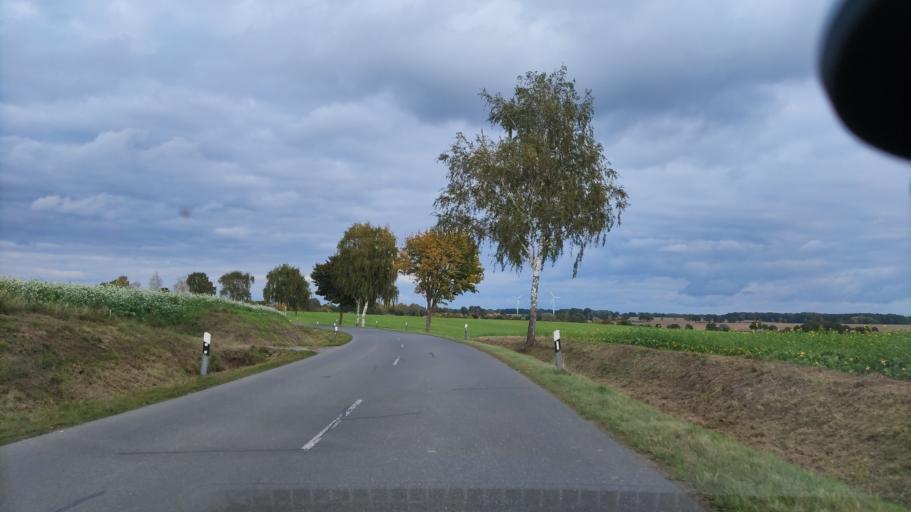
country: DE
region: Lower Saxony
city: Romstedt
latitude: 53.0885
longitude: 10.6468
